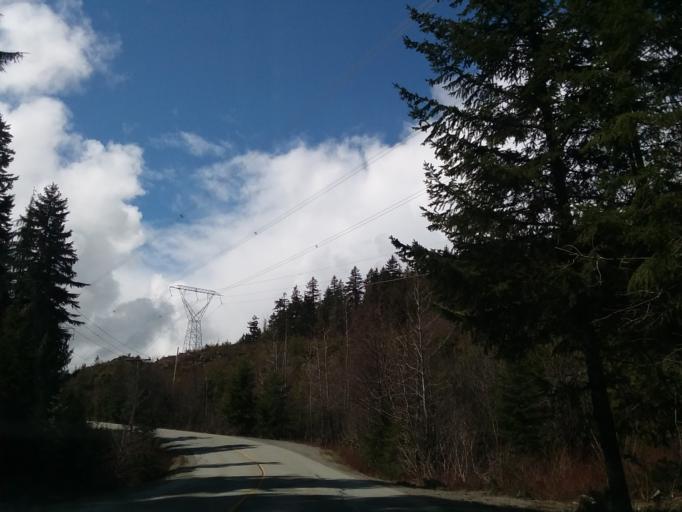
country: CA
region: British Columbia
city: Whistler
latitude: 50.1056
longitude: -122.9918
